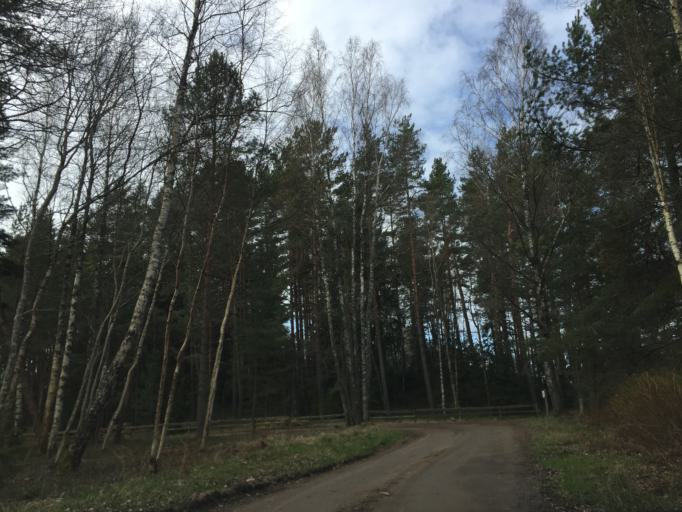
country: LV
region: Salacgrivas
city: Salacgriva
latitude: 57.5411
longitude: 24.3677
